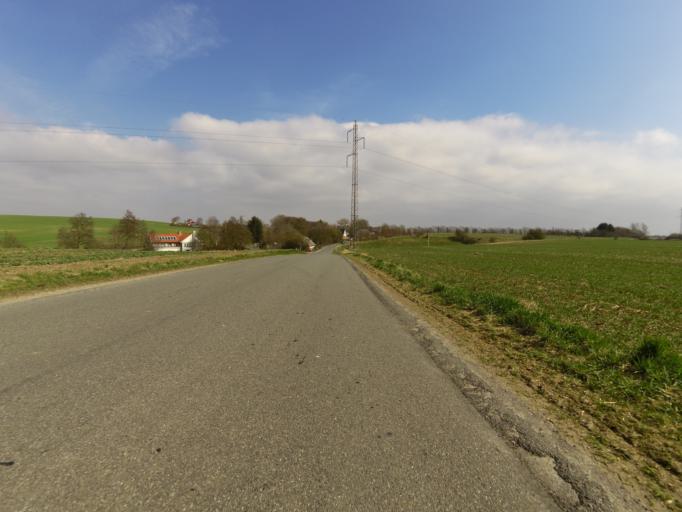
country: DK
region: Central Jutland
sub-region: Holstebro Kommune
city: Holstebro
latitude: 56.4385
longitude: 8.6535
